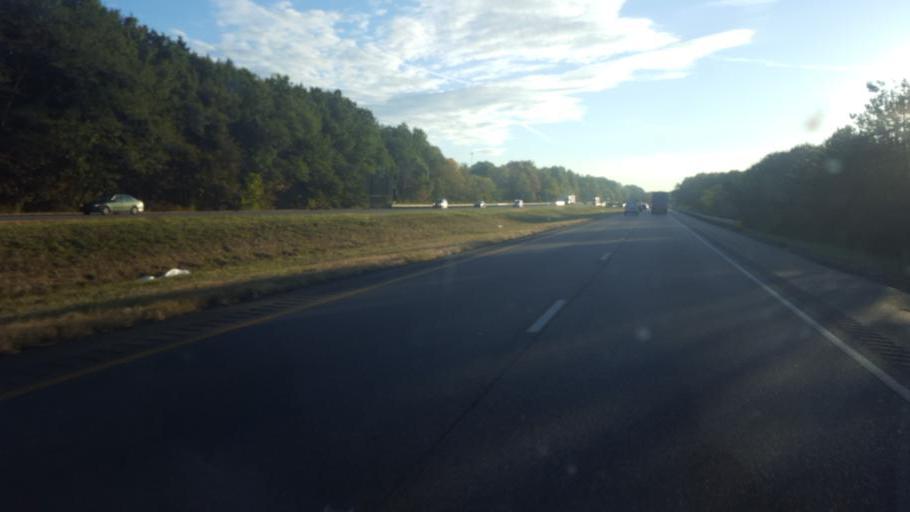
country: US
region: Ohio
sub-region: Trumbull County
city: Churchill
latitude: 41.1588
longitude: -80.6553
